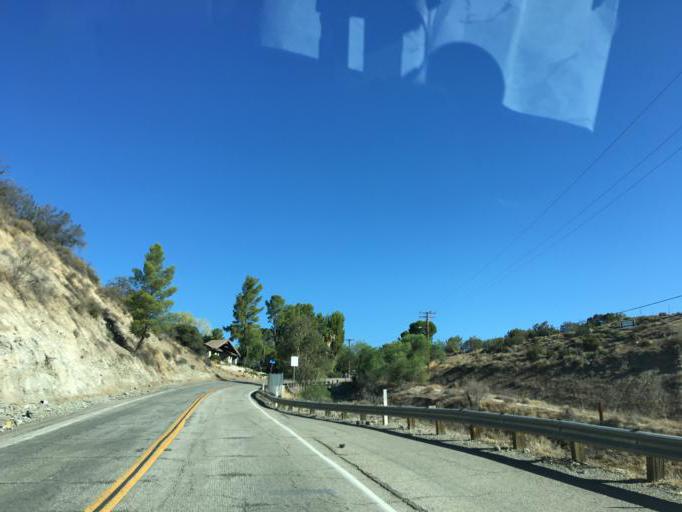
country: US
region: California
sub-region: Los Angeles County
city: Agua Dulce
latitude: 34.4774
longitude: -118.3305
